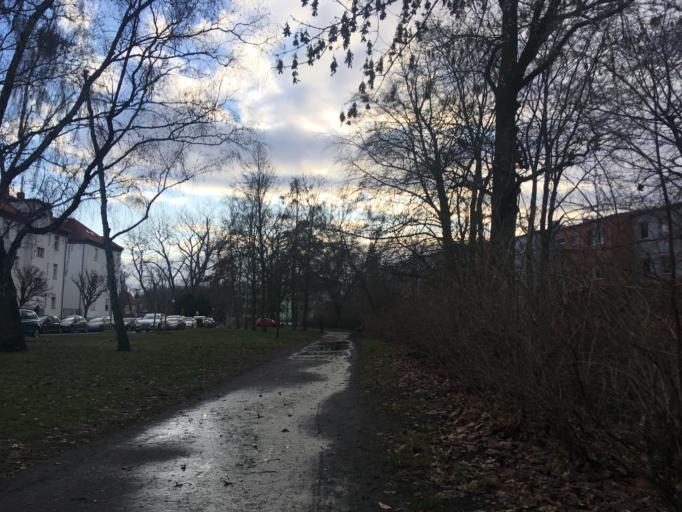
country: DE
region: Berlin
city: Wittenau
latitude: 52.5889
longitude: 13.3295
